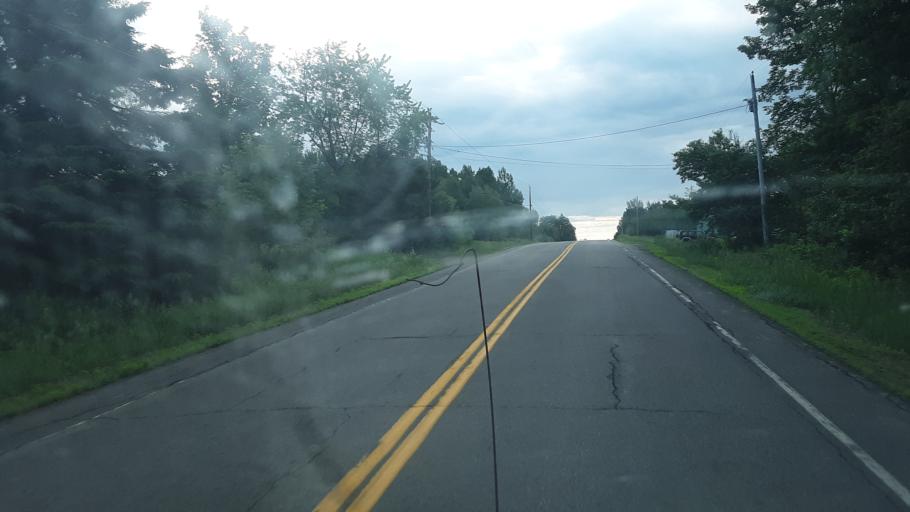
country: US
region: Maine
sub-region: Penobscot County
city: Patten
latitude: 45.8709
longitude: -68.3482
